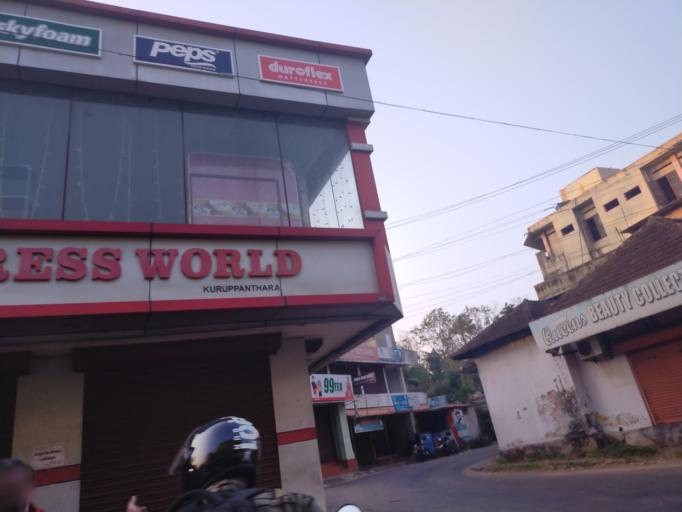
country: IN
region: Kerala
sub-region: Kottayam
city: Vaikam
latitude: 9.7335
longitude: 76.5058
